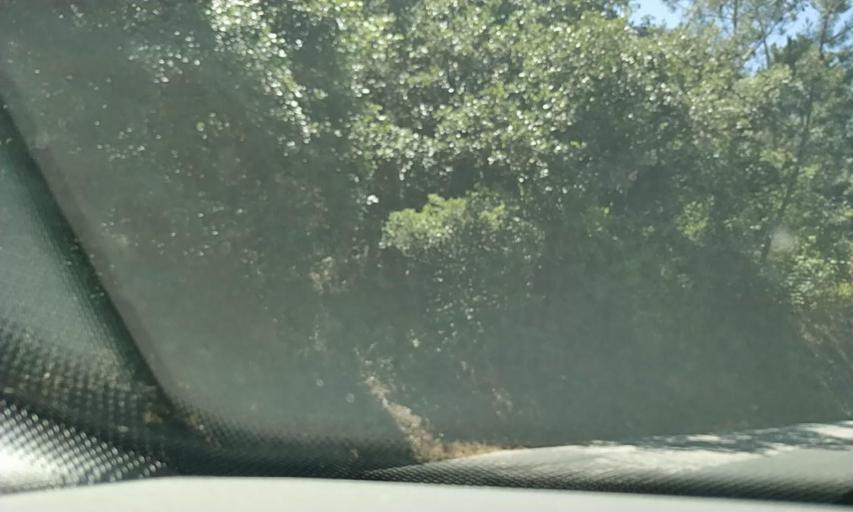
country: PT
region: Lisbon
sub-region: Sintra
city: Almargem
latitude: 38.8696
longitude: -9.2292
